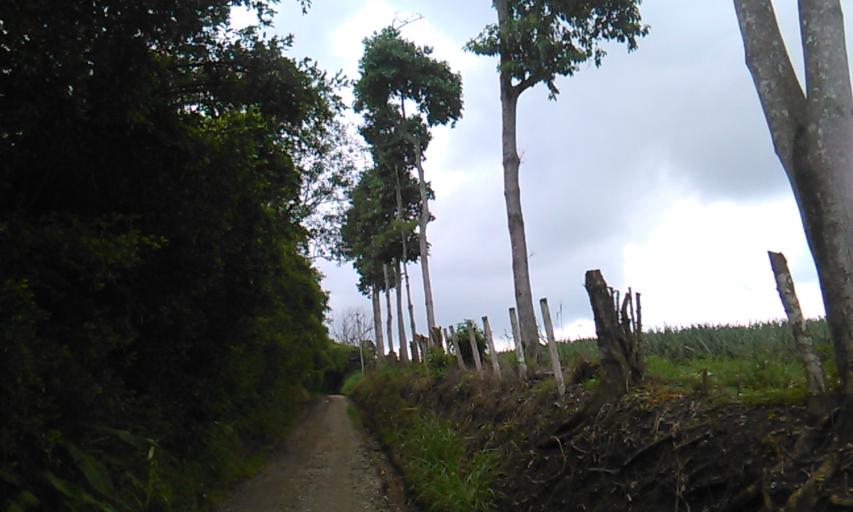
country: CO
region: Quindio
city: La Tebaida
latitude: 4.5054
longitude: -75.8581
